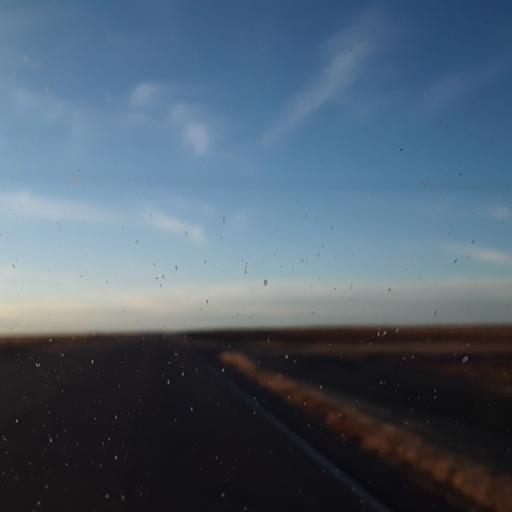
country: US
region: Colorado
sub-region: Cheyenne County
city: Cheyenne Wells
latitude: 38.8089
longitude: -102.4250
